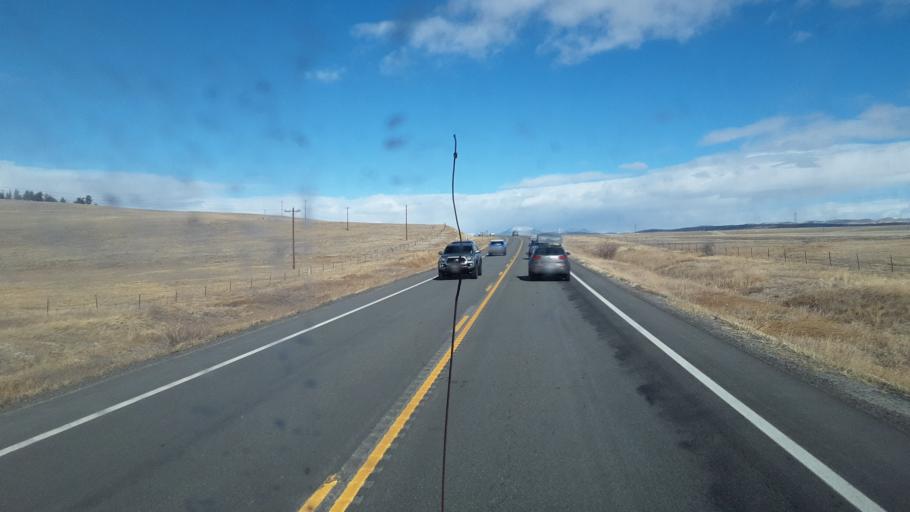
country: US
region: Colorado
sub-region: Park County
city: Fairplay
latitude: 39.0741
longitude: -105.9738
